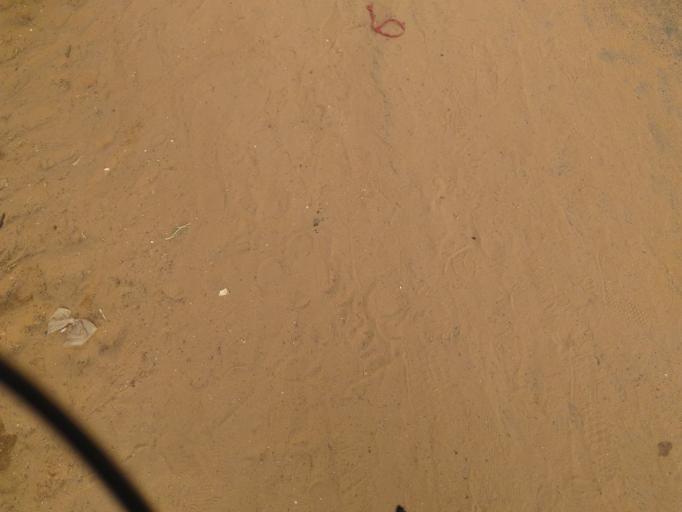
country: SN
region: Dakar
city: Pikine
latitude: 14.8021
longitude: -17.3394
